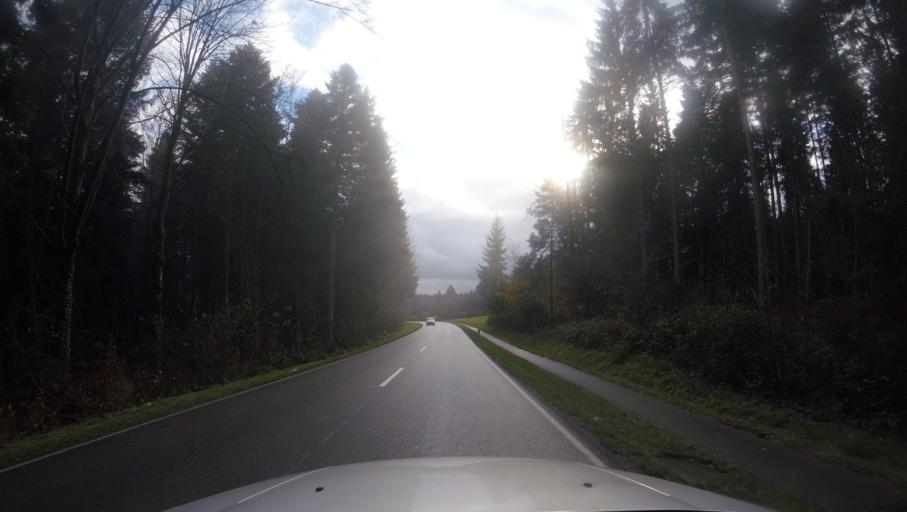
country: DE
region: Baden-Wuerttemberg
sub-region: Regierungsbezirk Stuttgart
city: Spraitbach
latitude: 48.8634
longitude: 9.7634
